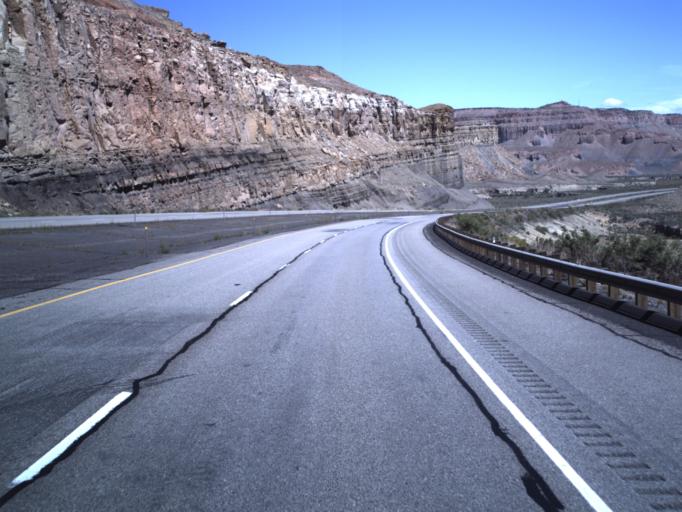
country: US
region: Utah
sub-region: Emery County
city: Ferron
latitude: 38.8040
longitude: -111.2641
